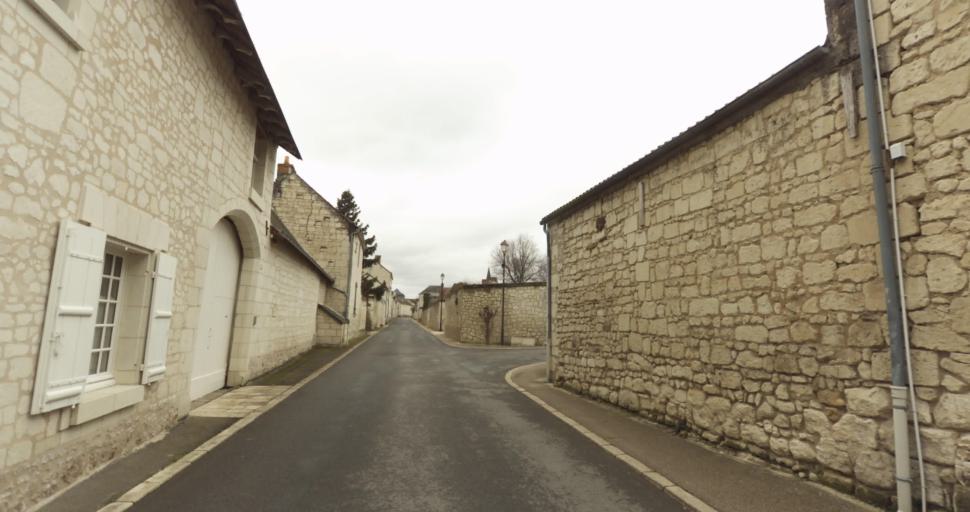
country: FR
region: Pays de la Loire
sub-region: Departement de Maine-et-Loire
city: Chace
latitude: 47.2144
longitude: -0.0723
